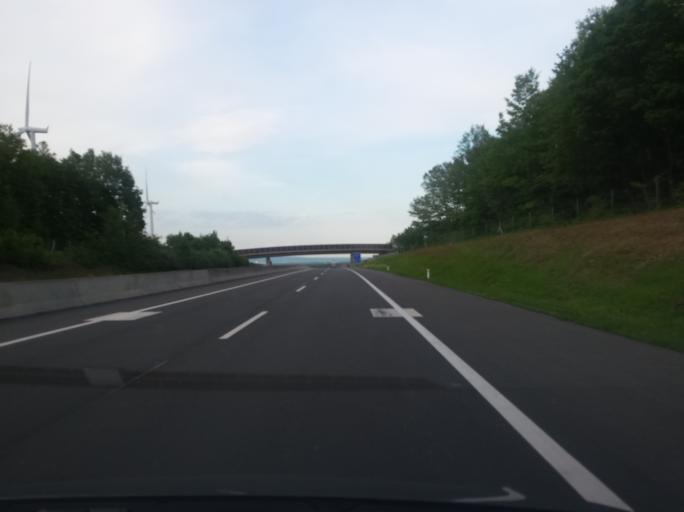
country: AT
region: Burgenland
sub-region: Politischer Bezirk Mattersburg
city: Pottelsdorf
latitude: 47.7592
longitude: 16.4134
